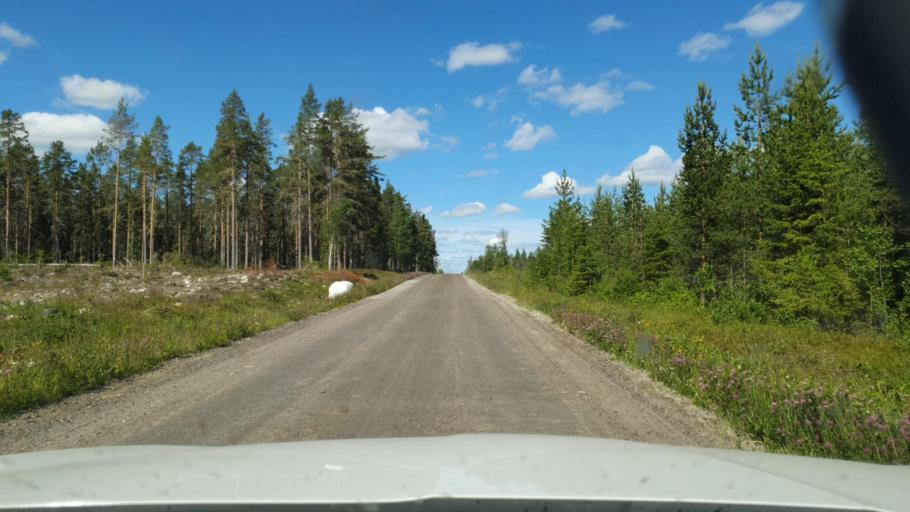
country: SE
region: Vaesterbotten
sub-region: Skelleftea Kommun
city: Byske
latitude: 65.1325
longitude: 21.1949
